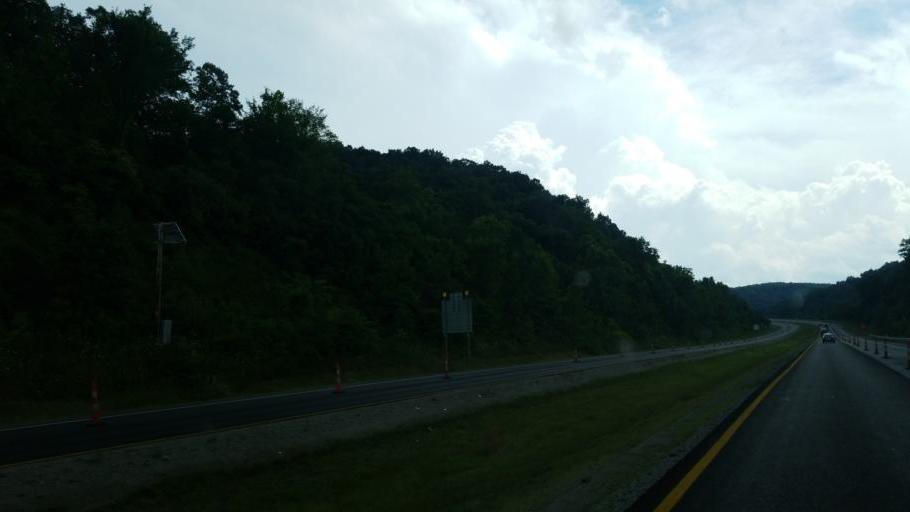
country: US
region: West Virginia
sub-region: Kanawha County
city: Alum Creek
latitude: 38.2610
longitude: -81.8342
